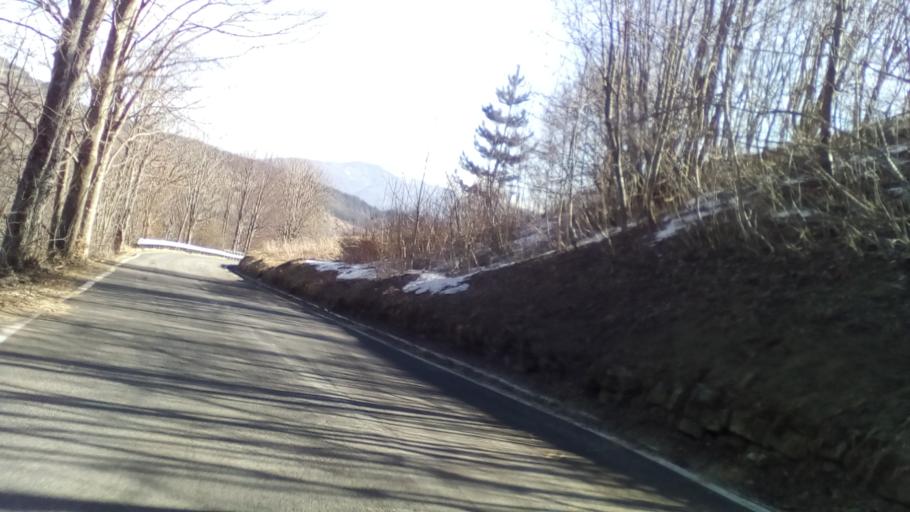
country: IT
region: Emilia-Romagna
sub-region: Provincia di Modena
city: Pievepelago
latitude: 44.1967
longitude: 10.5373
